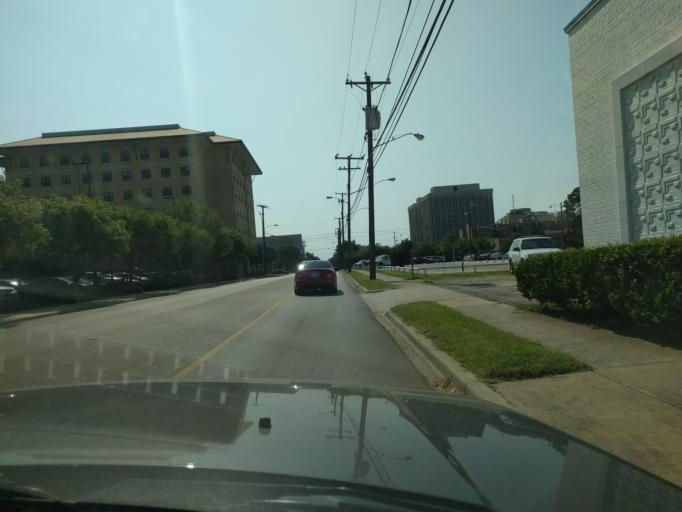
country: US
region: Texas
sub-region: Dallas County
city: Dallas
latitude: 32.7940
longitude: -96.7817
